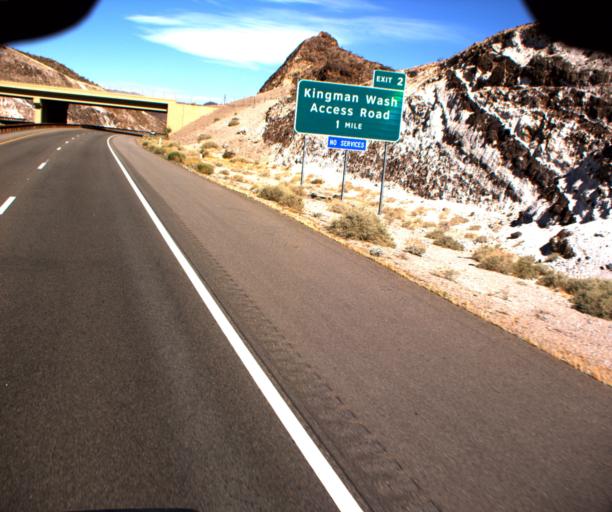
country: US
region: Nevada
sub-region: Clark County
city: Boulder City
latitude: 35.9847
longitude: -114.7098
